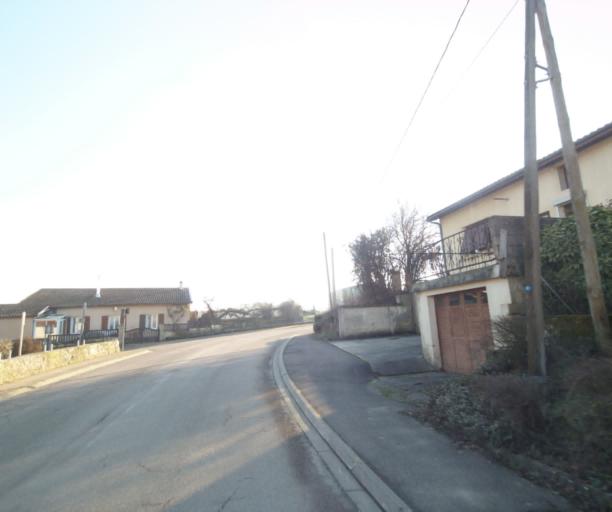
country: FR
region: Champagne-Ardenne
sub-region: Departement de la Haute-Marne
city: Bienville
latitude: 48.5809
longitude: 5.0885
